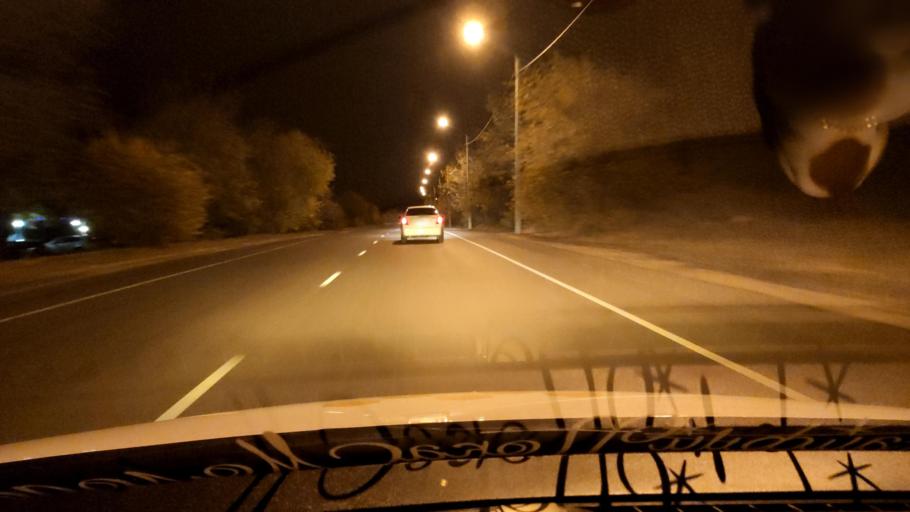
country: RU
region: Voronezj
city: Voronezh
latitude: 51.6114
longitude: 39.1793
